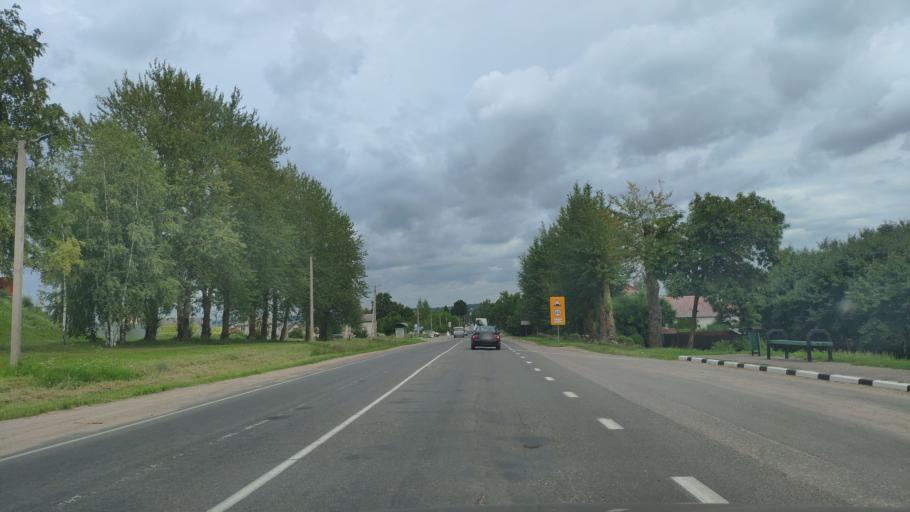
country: BY
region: Minsk
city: Zaslawye
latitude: 53.9939
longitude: 27.2691
